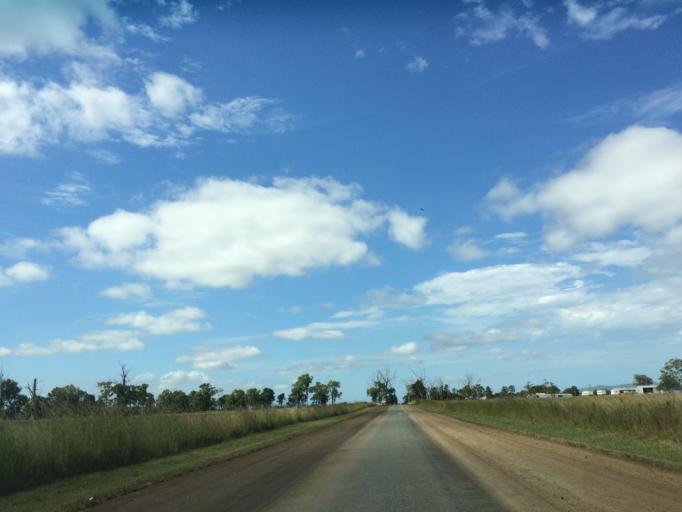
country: AU
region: Queensland
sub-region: Logan
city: Cedar Vale
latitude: -27.8753
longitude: 152.9562
